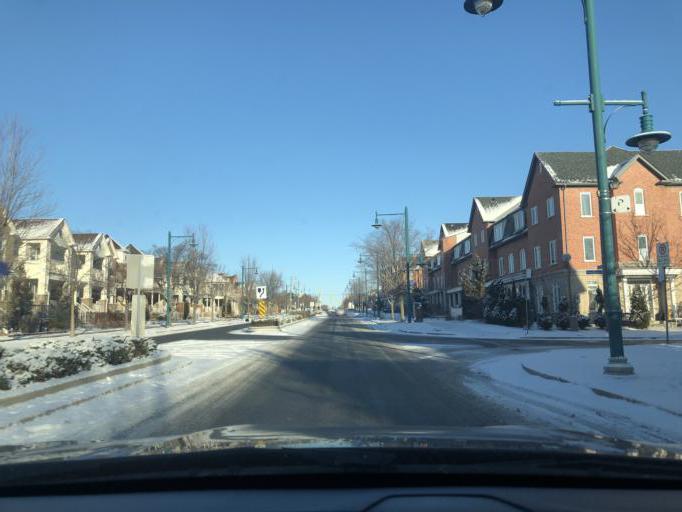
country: CA
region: Ontario
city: Scarborough
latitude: 43.7778
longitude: -79.1358
